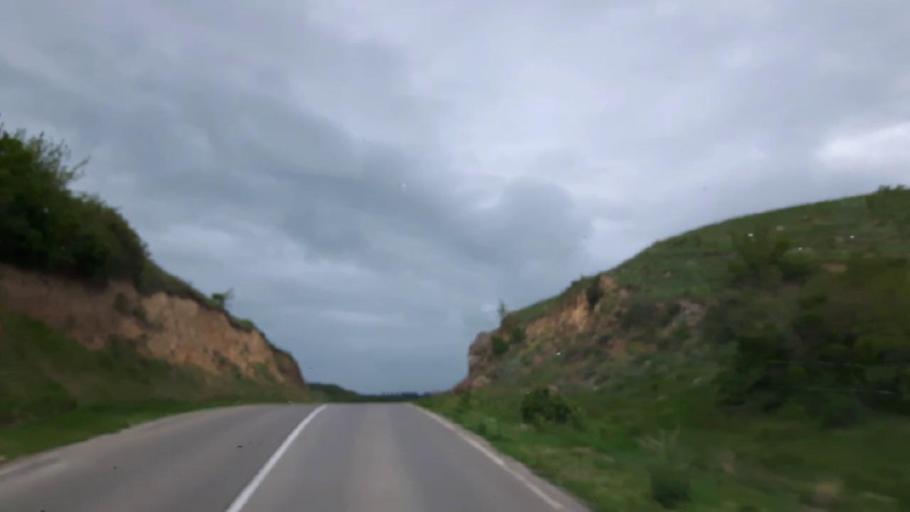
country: GE
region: Shida Kartli
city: Gori
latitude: 41.9907
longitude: 44.0385
